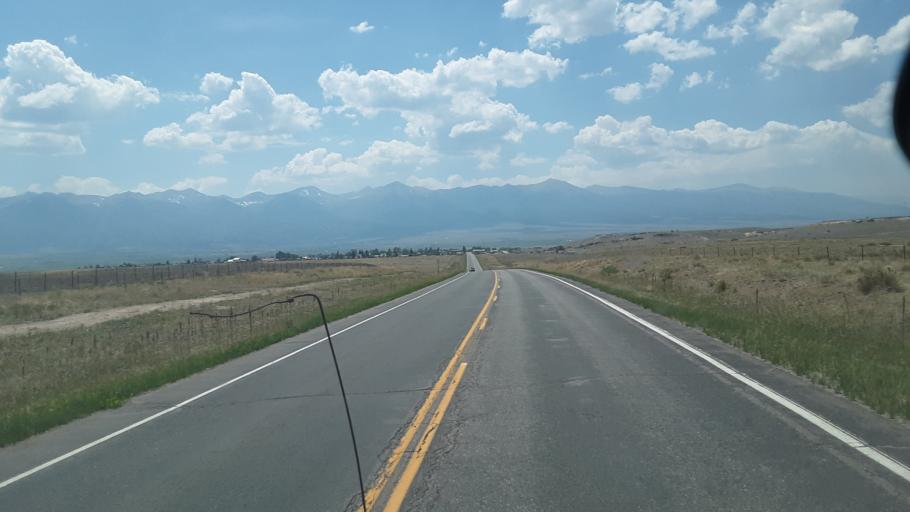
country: US
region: Colorado
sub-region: Custer County
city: Westcliffe
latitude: 38.1358
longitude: -105.4252
